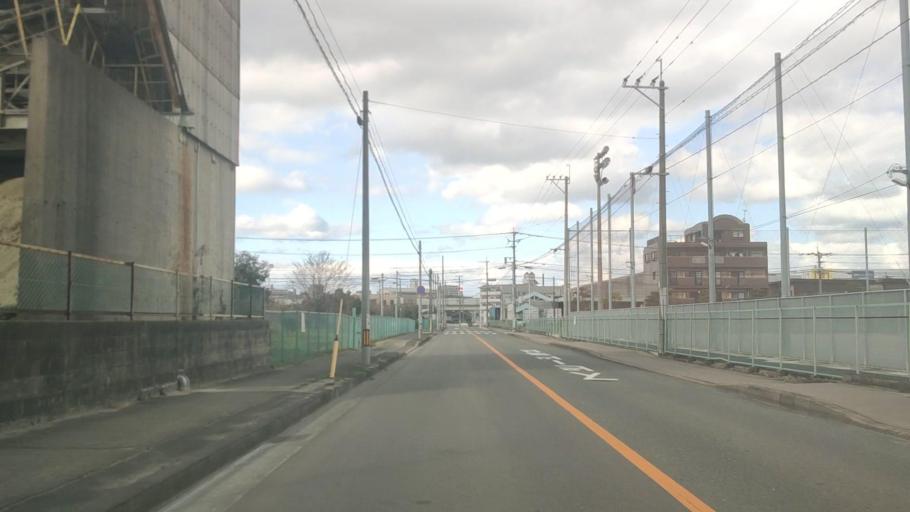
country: JP
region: Fukuoka
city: Fukuoka-shi
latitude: 33.6107
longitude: 130.4338
